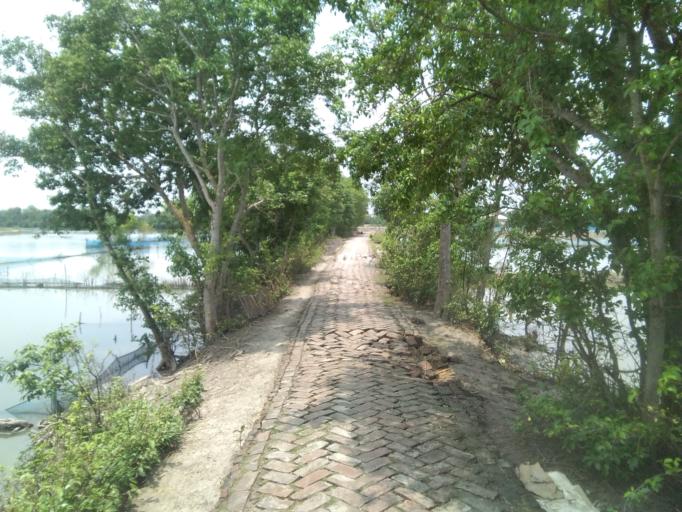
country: BD
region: Khulna
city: Phultala
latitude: 22.6399
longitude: 89.4027
